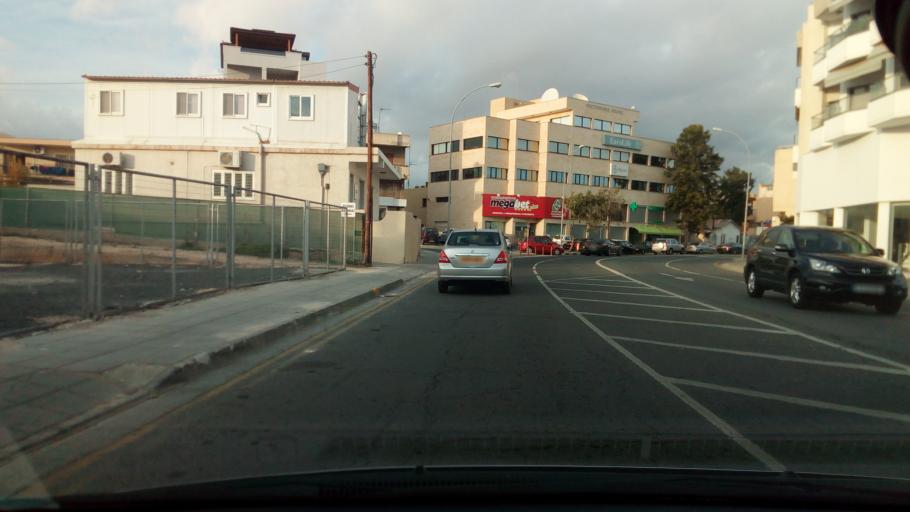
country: CY
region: Limassol
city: Limassol
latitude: 34.7007
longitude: 33.0458
